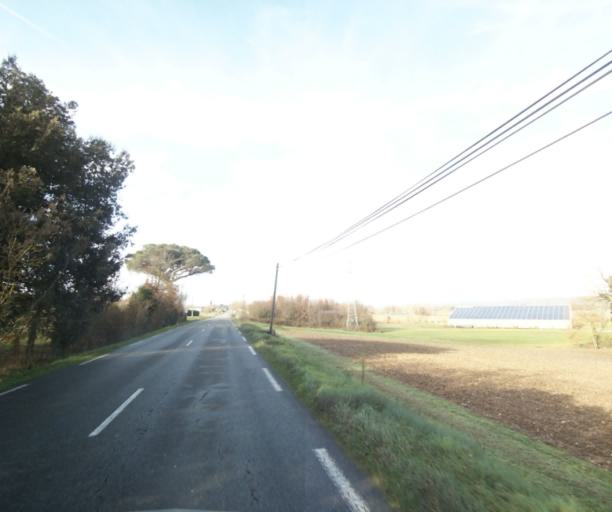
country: FR
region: Midi-Pyrenees
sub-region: Departement de la Haute-Garonne
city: Villemur-sur-Tarn
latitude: 43.8642
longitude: 1.4765
